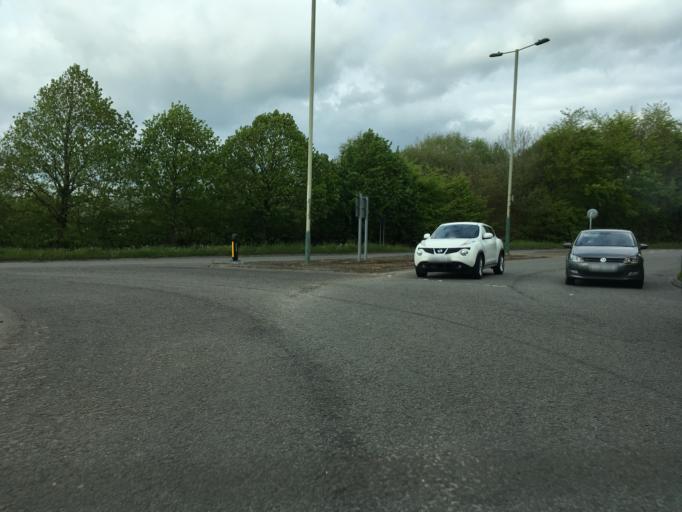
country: GB
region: Wales
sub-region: Caerphilly County Borough
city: Nelson
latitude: 51.6503
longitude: -3.2773
